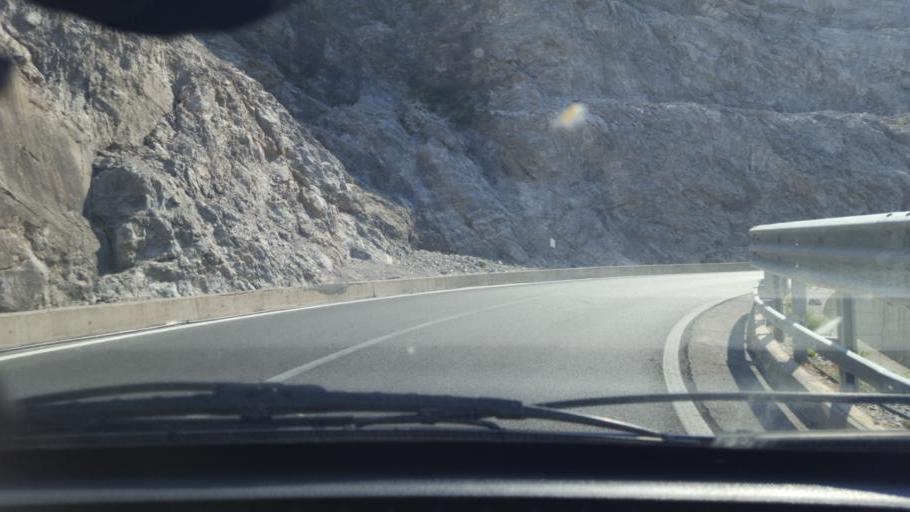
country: AL
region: Shkoder
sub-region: Rrethi i Malesia e Madhe
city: Kastrat
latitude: 42.4136
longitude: 19.5112
